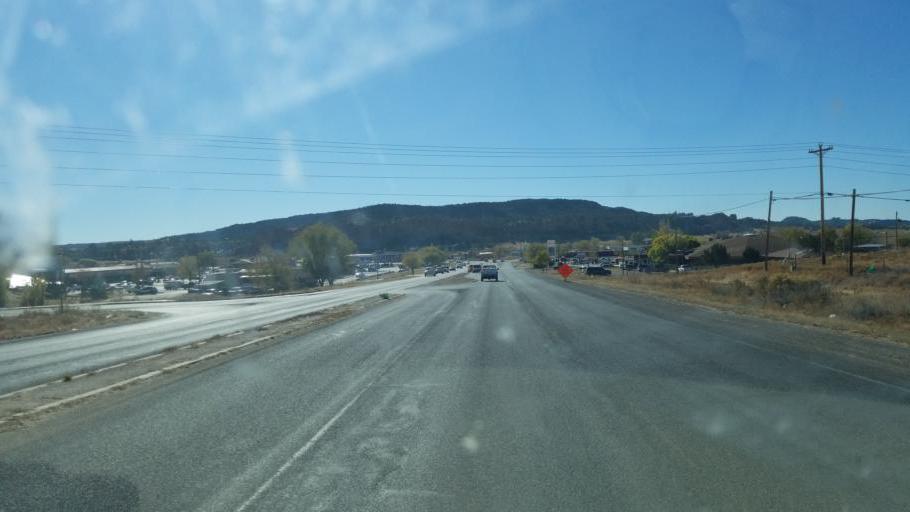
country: US
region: Arizona
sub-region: Apache County
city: Window Rock
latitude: 35.6674
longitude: -109.0580
